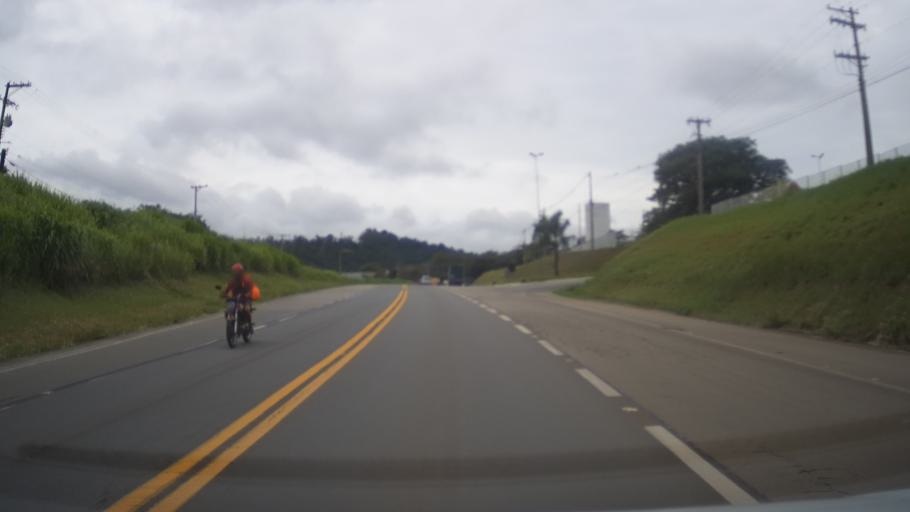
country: BR
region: Sao Paulo
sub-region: Vinhedo
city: Vinhedo
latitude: -23.0589
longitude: -47.0353
